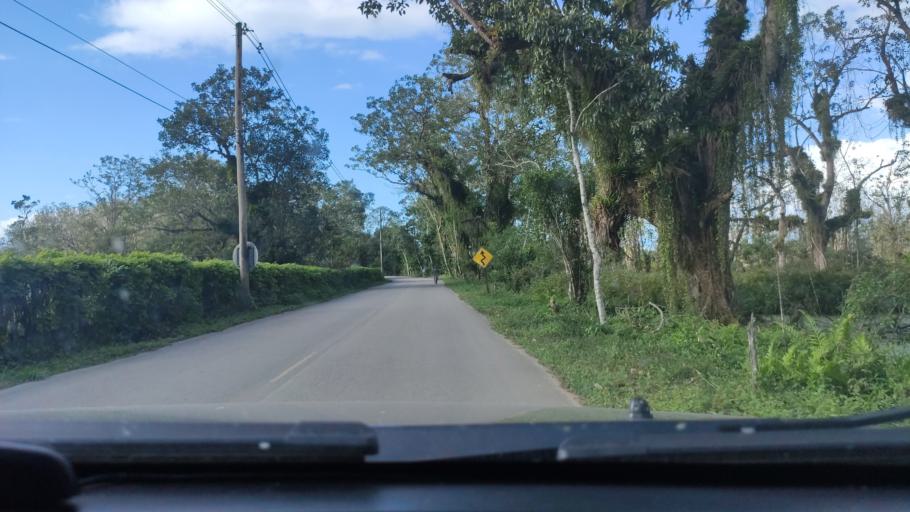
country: BR
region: Sao Paulo
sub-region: Sao Sebastiao
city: Sao Sebastiao
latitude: -23.6978
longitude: -45.4679
